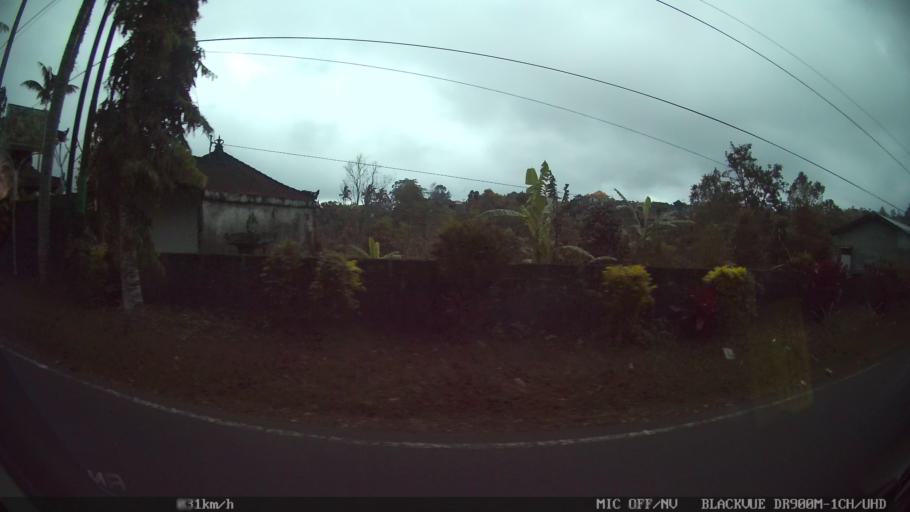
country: ID
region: Bali
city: Klau
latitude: -8.3313
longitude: 115.0321
